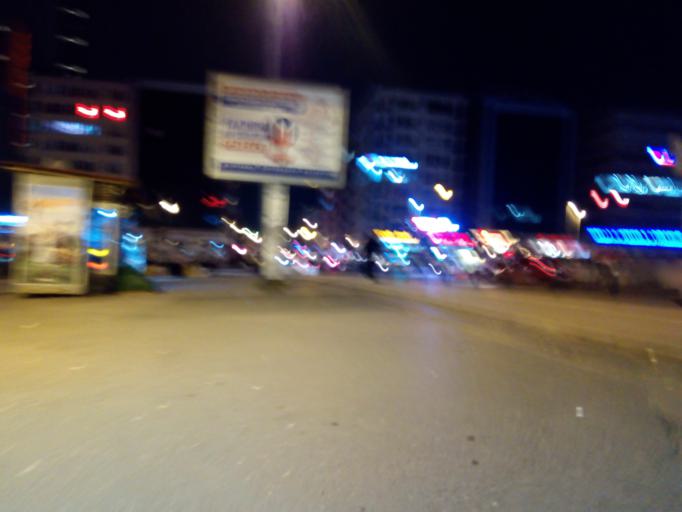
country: TR
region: Istanbul
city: Sisli
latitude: 41.0713
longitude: 28.9989
